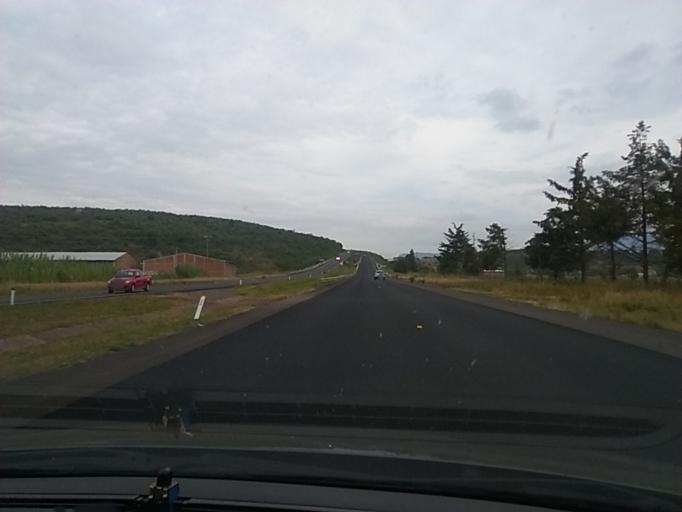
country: MX
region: Mexico
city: Huaniqueo de Morales
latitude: 19.8956
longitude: -101.5691
